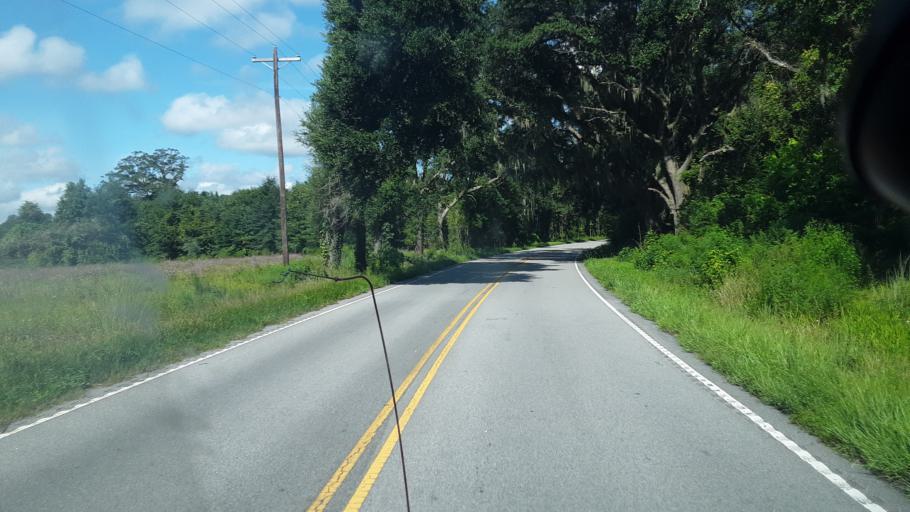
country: US
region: South Carolina
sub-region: Jasper County
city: Ridgeland
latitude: 32.5918
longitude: -80.9780
